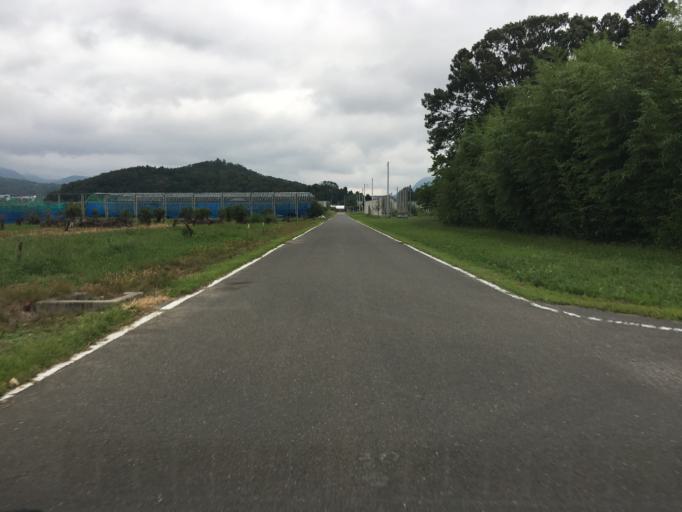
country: JP
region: Fukushima
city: Fukushima-shi
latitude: 37.8096
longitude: 140.4295
